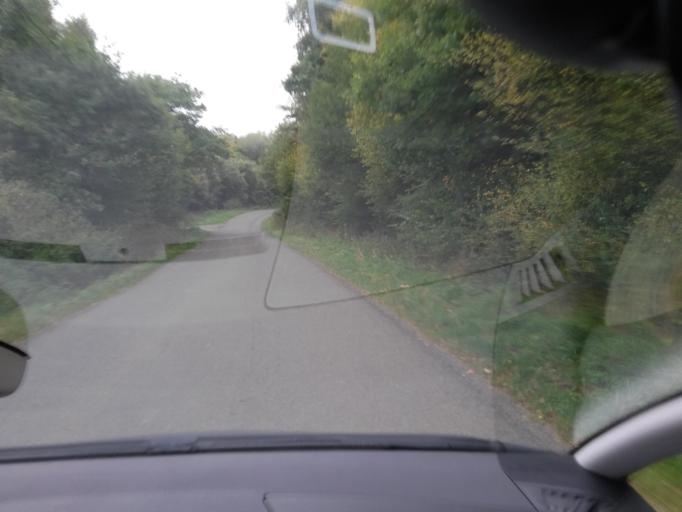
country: BE
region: Wallonia
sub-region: Province du Luxembourg
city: Attert
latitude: 49.7152
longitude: 5.7405
